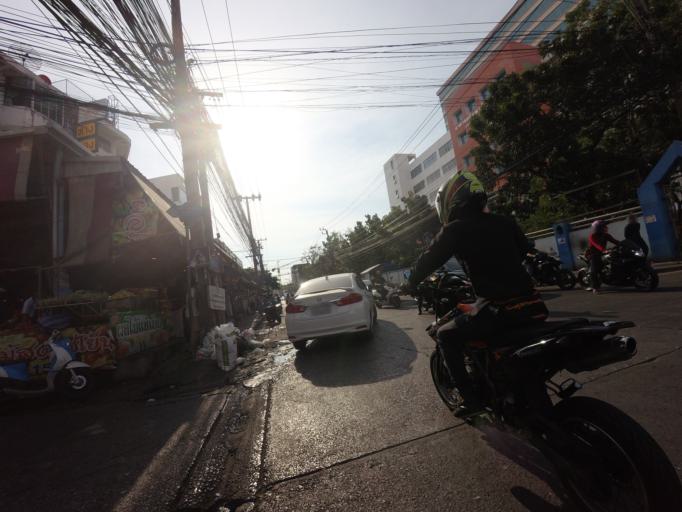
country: TH
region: Bangkok
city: Bang Kapi
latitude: 13.7532
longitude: 100.6206
